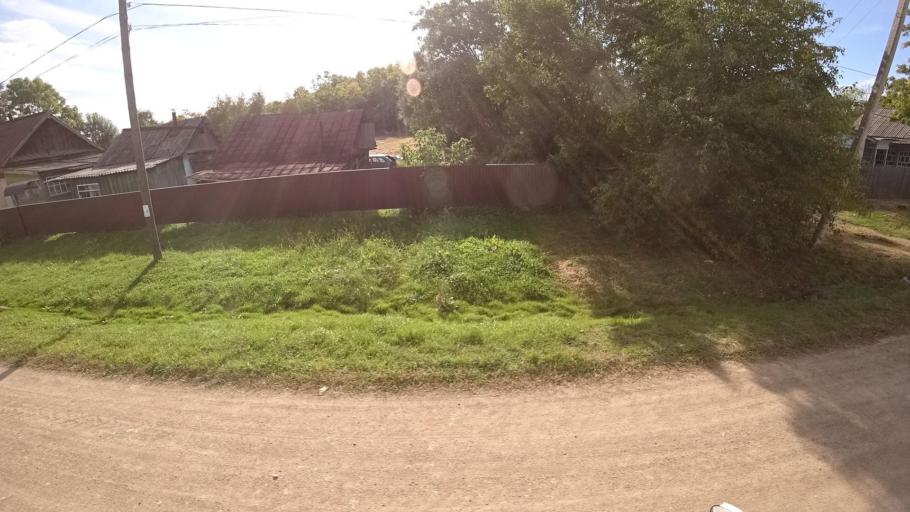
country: RU
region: Primorskiy
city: Dostoyevka
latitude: 44.3001
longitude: 133.4596
